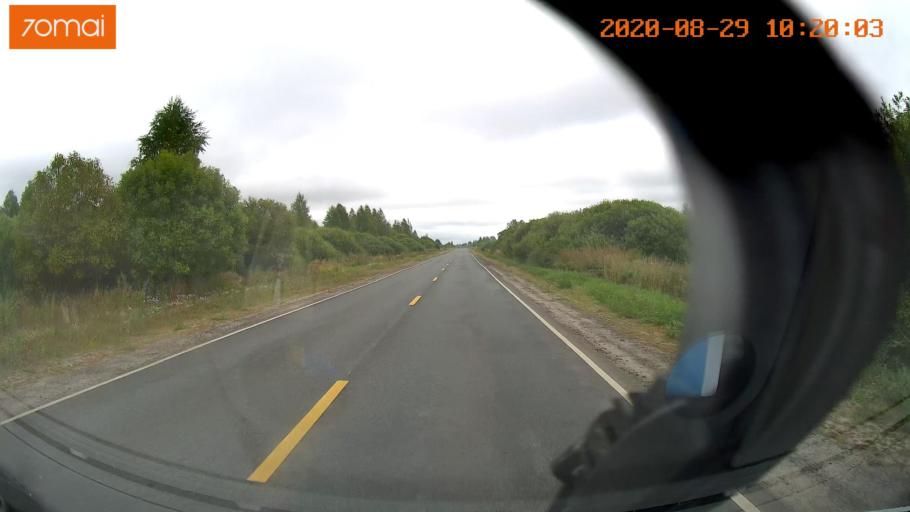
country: RU
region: Ivanovo
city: Yur'yevets
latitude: 57.3253
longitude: 42.8749
